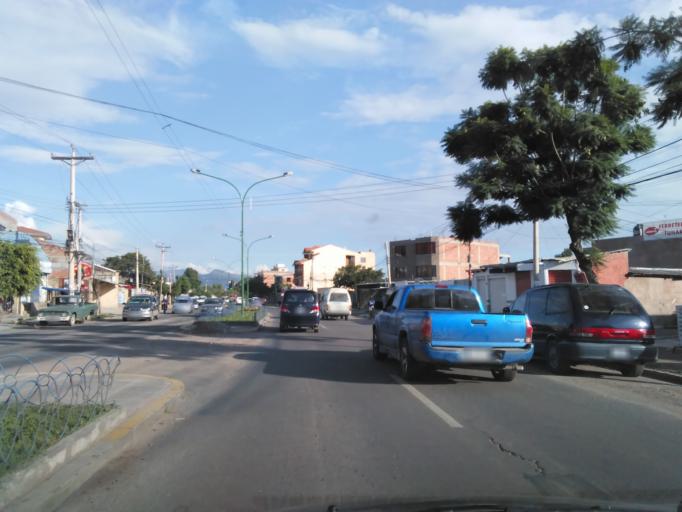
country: BO
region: Cochabamba
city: Cochabamba
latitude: -17.3626
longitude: -66.1812
